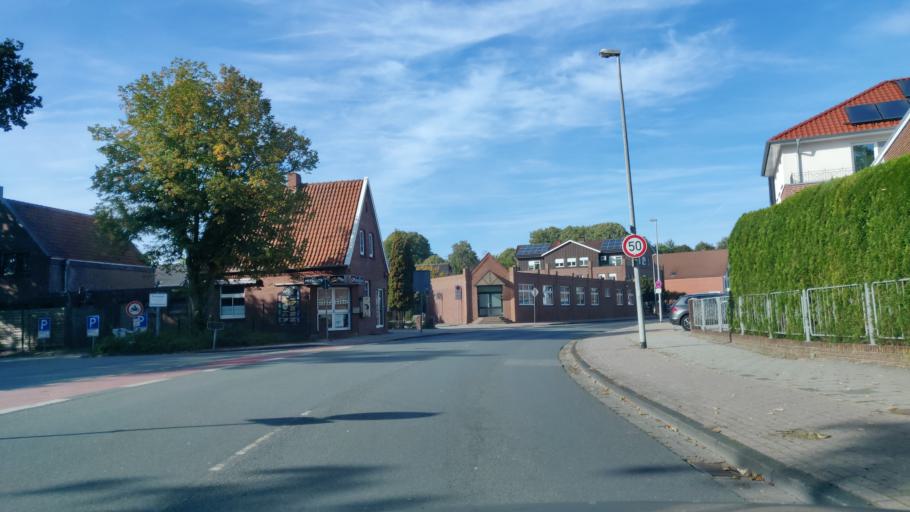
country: DE
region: Lower Saxony
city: Leer
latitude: 53.2274
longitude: 7.4422
